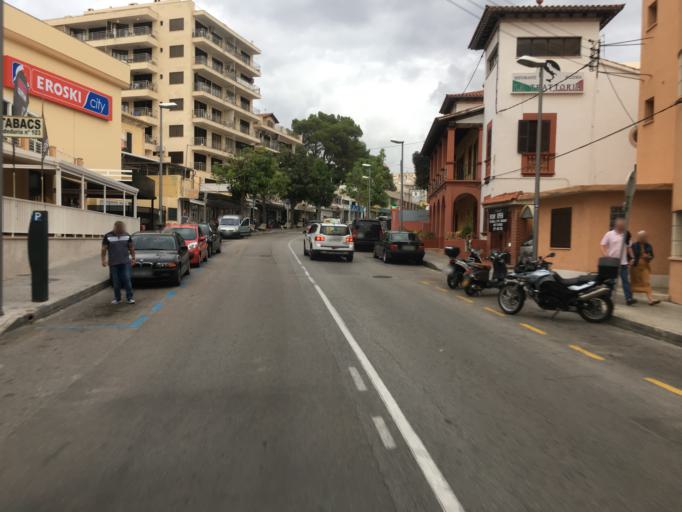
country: ES
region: Balearic Islands
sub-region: Illes Balears
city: Palma
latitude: 39.5512
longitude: 2.6002
